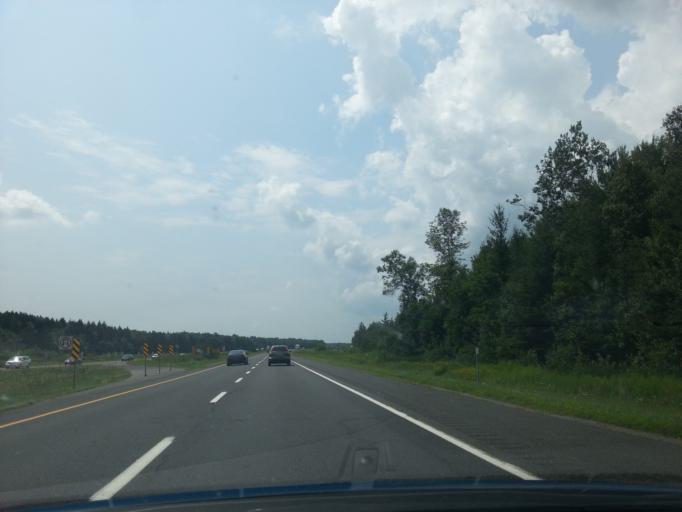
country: CA
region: Quebec
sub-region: Chaudiere-Appalaches
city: Saint-Antoine-de-Tilly
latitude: 46.5562
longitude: -71.5942
